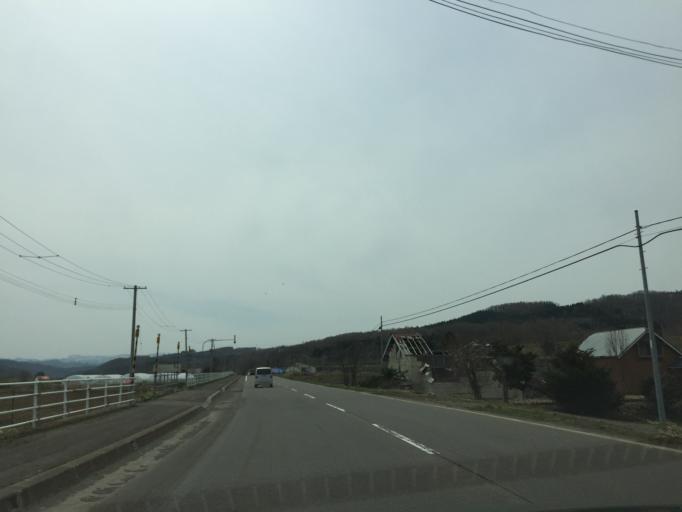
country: JP
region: Hokkaido
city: Ashibetsu
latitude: 43.5938
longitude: 142.1989
